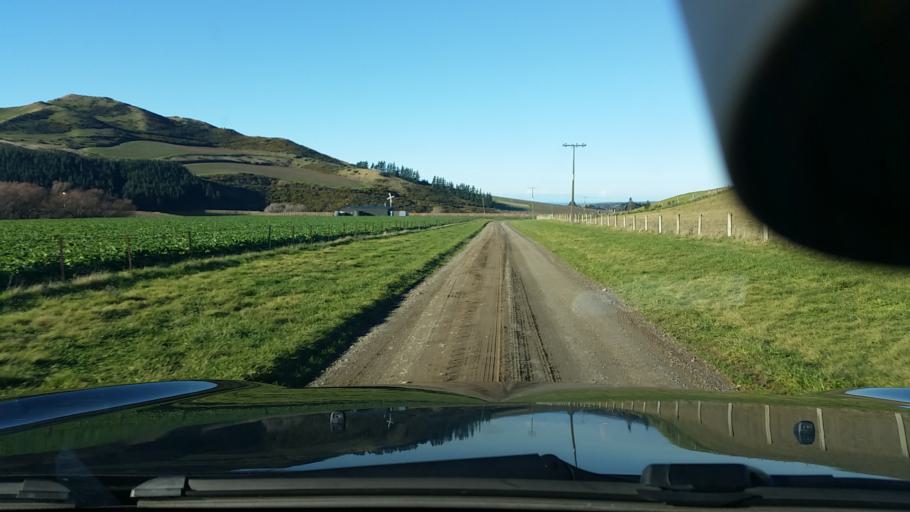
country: NZ
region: Marlborough
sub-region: Marlborough District
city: Blenheim
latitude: -41.6384
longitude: 174.0277
